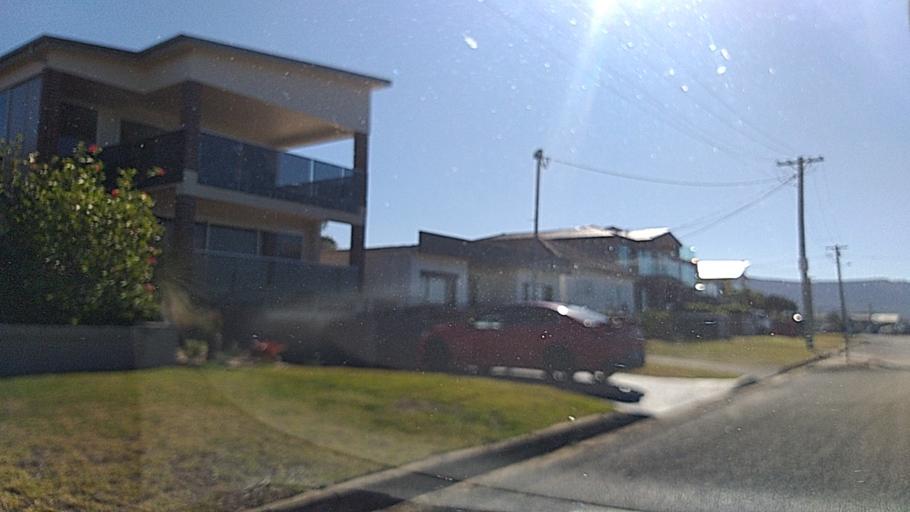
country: AU
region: New South Wales
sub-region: Wollongong
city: Bulli
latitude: -34.3532
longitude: 150.9190
